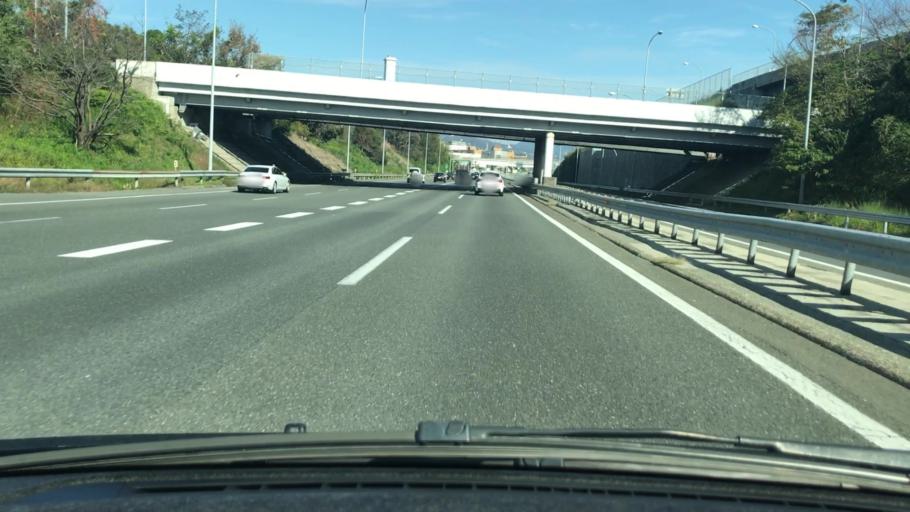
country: JP
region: Osaka
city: Ibaraki
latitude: 34.8035
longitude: 135.5415
